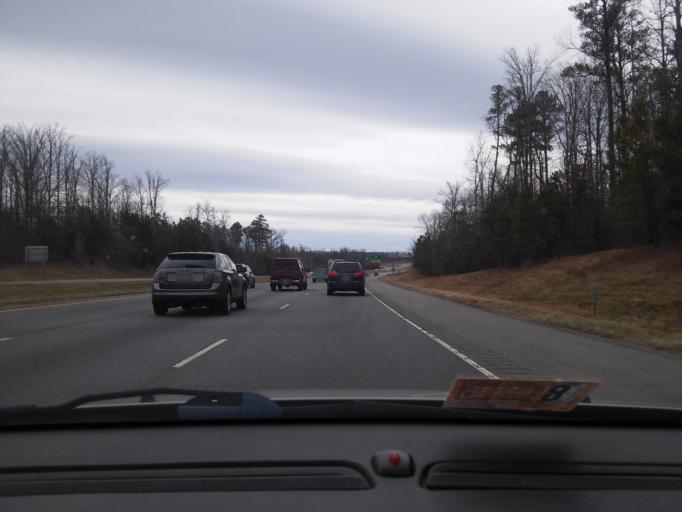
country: US
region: Virginia
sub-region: Henrico County
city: Short Pump
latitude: 37.6540
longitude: -77.6637
